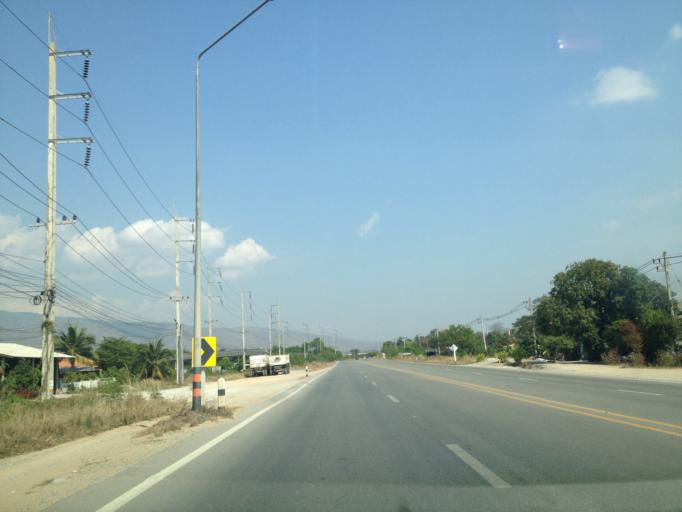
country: TH
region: Chiang Mai
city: Hot
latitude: 18.2784
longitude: 98.6378
